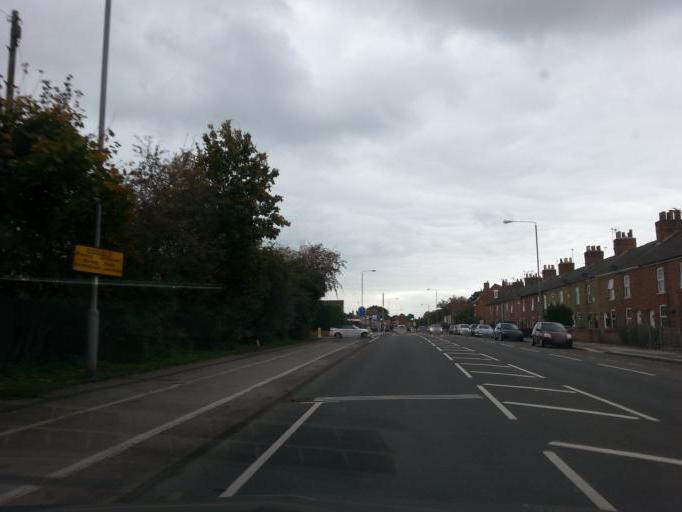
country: GB
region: England
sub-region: Nottinghamshire
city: Newark on Trent
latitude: 53.0597
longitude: -0.7865
